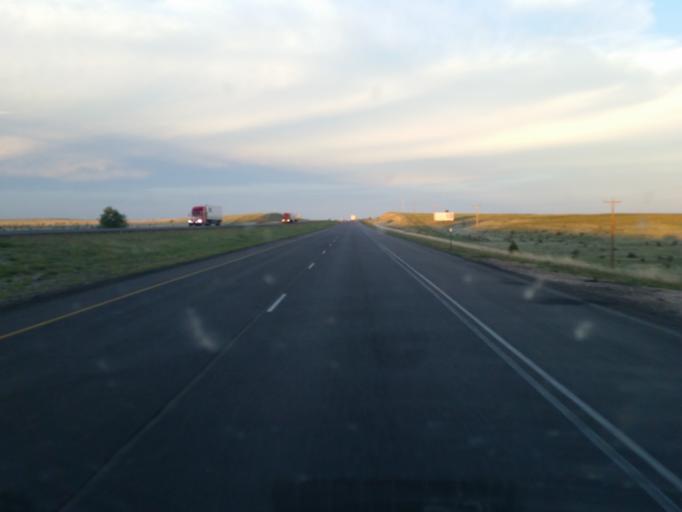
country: US
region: New Mexico
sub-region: Guadalupe County
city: Santa Rosa
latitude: 34.9901
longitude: -105.2675
